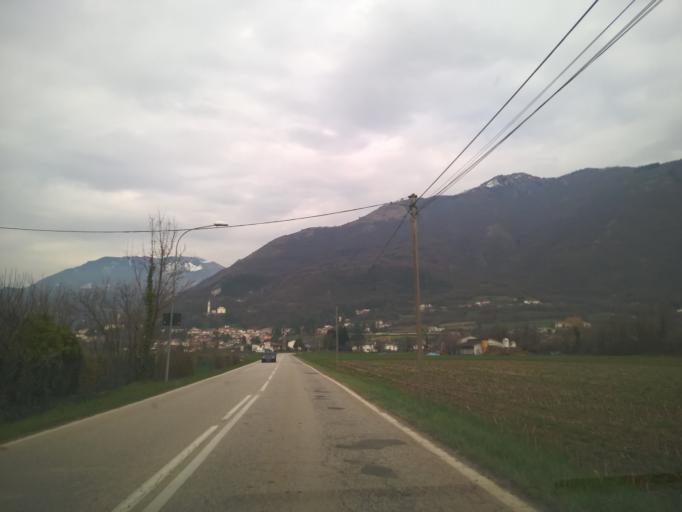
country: IT
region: Veneto
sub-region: Provincia di Vicenza
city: Santorso
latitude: 45.7313
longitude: 11.4113
